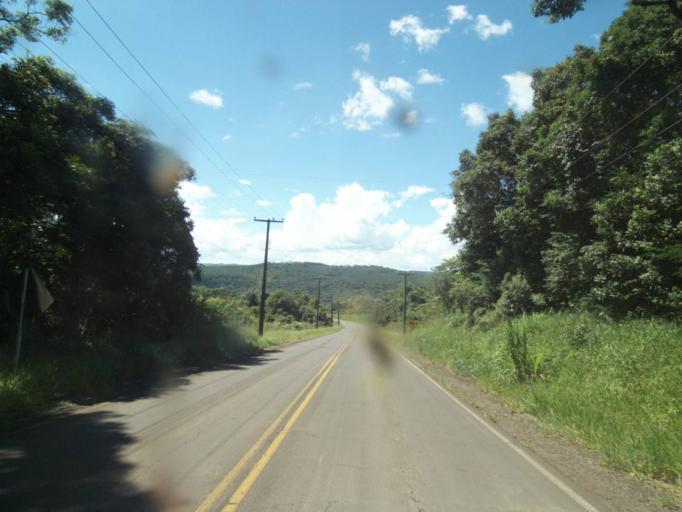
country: BR
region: Parana
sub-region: Chopinzinho
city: Chopinzinho
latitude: -25.7820
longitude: -52.1012
